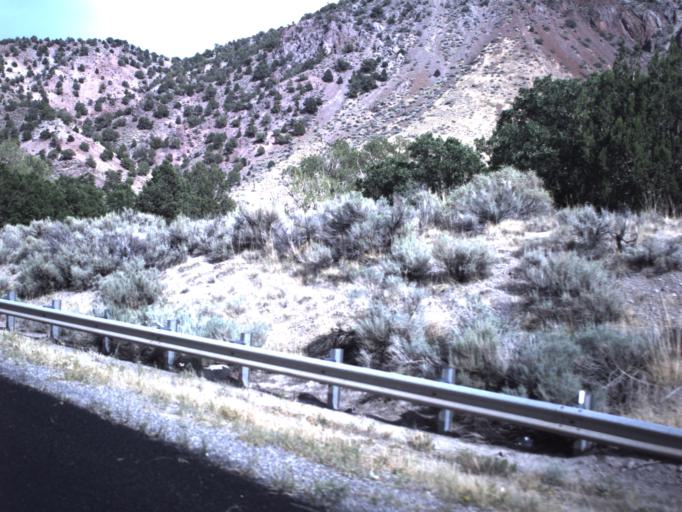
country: US
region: Utah
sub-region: Sevier County
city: Monroe
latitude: 38.5640
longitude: -112.2701
